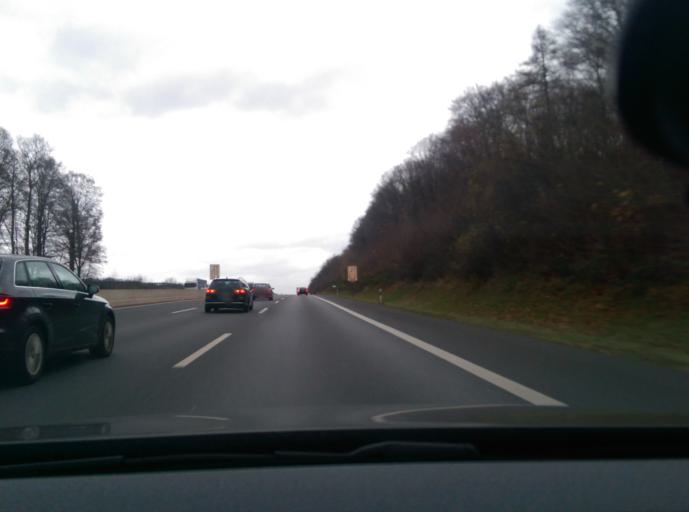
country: DE
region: Lower Saxony
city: Hillerse
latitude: 51.6660
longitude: 9.9191
